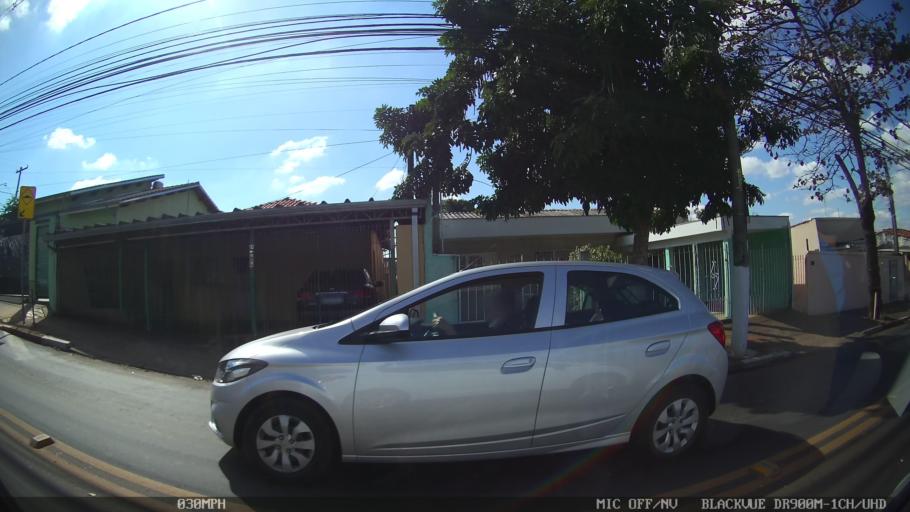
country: BR
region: Sao Paulo
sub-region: Hortolandia
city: Hortolandia
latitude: -22.8796
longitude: -47.2234
